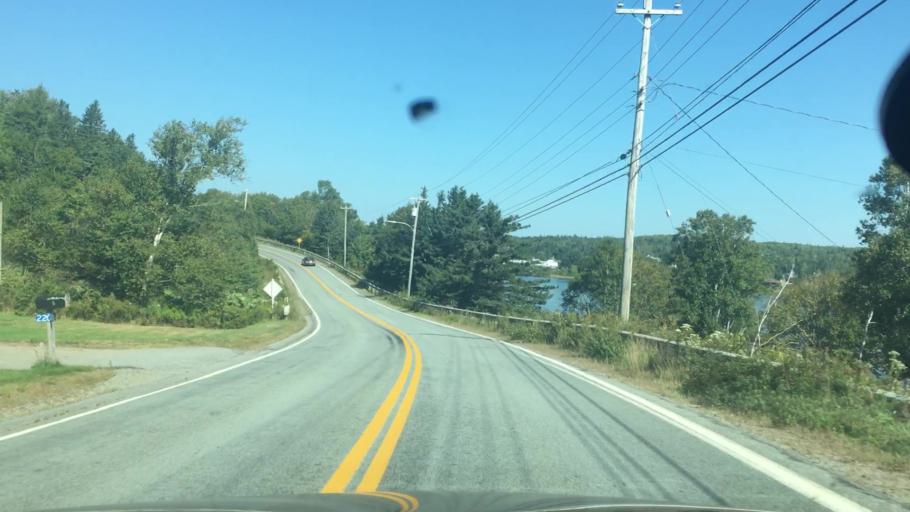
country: CA
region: Nova Scotia
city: New Glasgow
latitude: 44.9155
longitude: -62.5386
